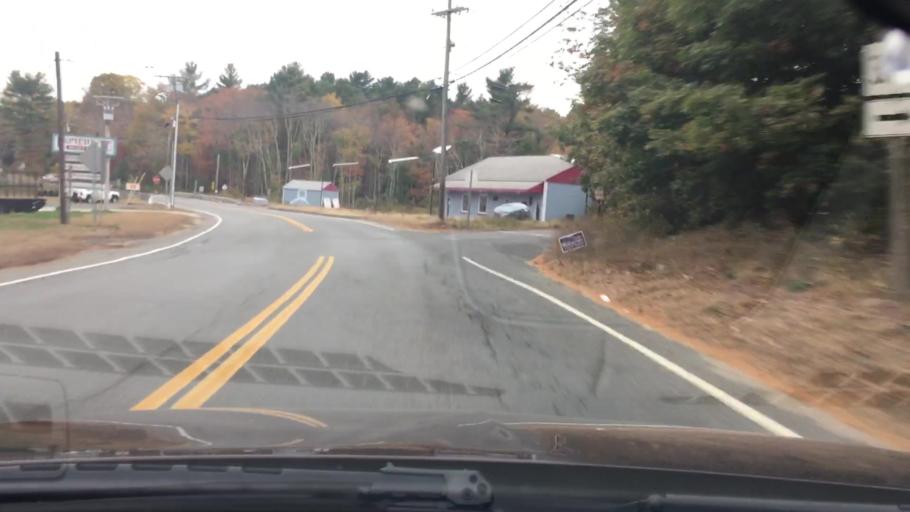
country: US
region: Connecticut
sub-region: Tolland County
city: Stafford Springs
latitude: 41.9715
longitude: -72.3344
